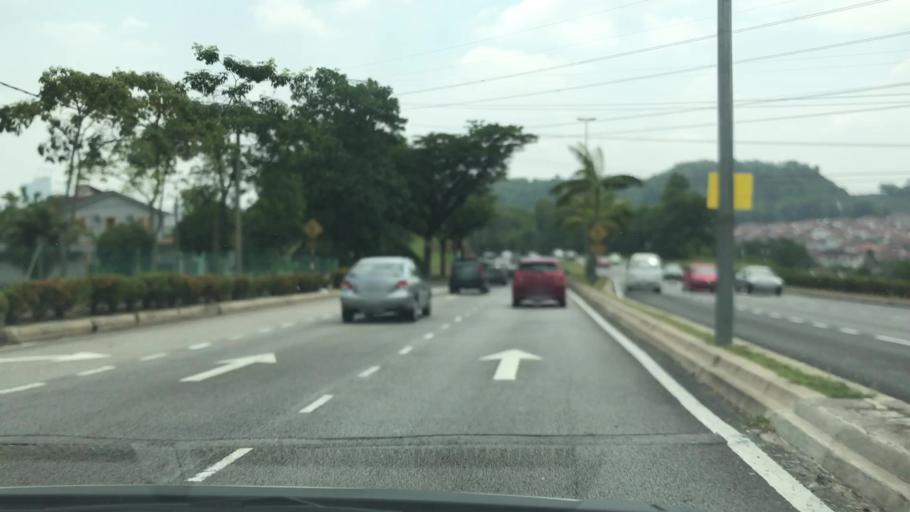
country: MY
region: Selangor
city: Kampong Baharu Balakong
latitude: 3.0277
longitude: 101.6804
